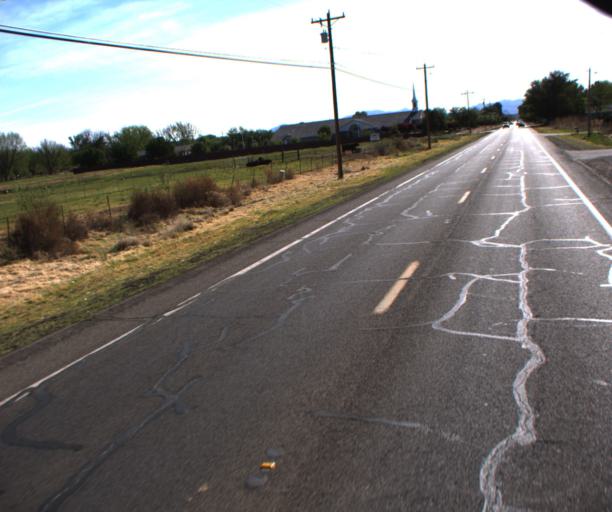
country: US
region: Arizona
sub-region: Cochise County
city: Saint David
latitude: 31.9053
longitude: -110.2385
